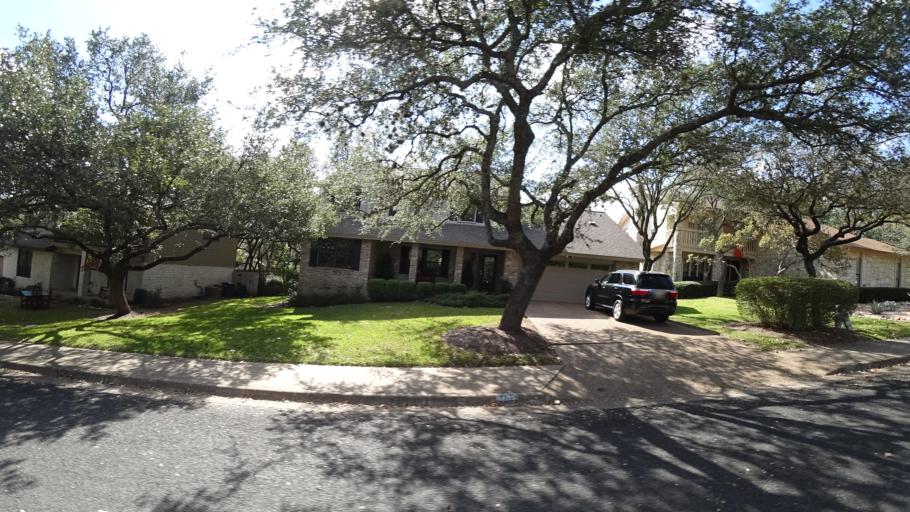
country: US
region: Texas
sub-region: Williamson County
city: Anderson Mill
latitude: 30.4241
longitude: -97.8034
